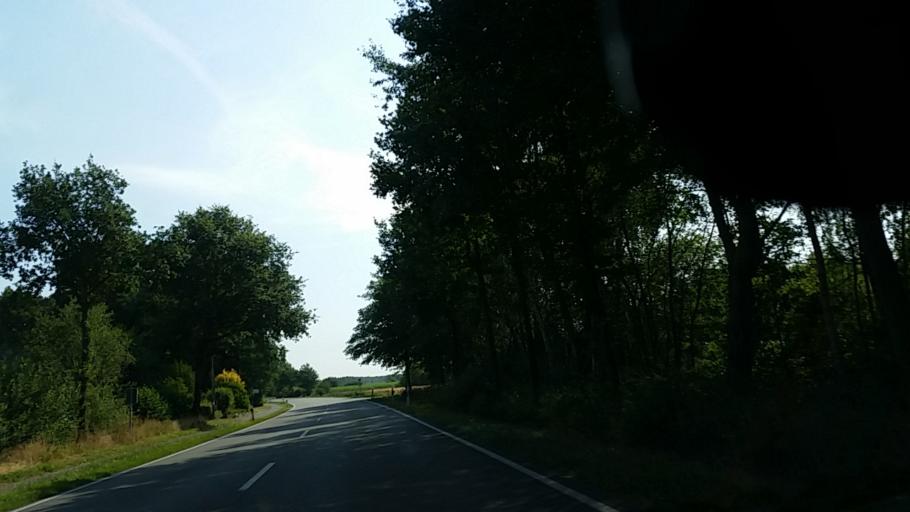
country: DE
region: Lower Saxony
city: Steinfeld
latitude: 52.5998
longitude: 8.2740
